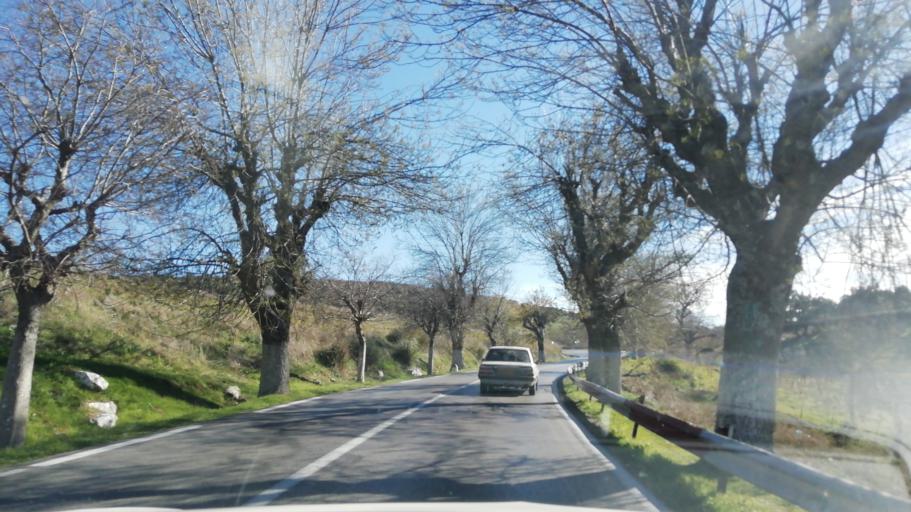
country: DZ
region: Tlemcen
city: Mansoura
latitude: 34.8338
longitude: -1.3720
